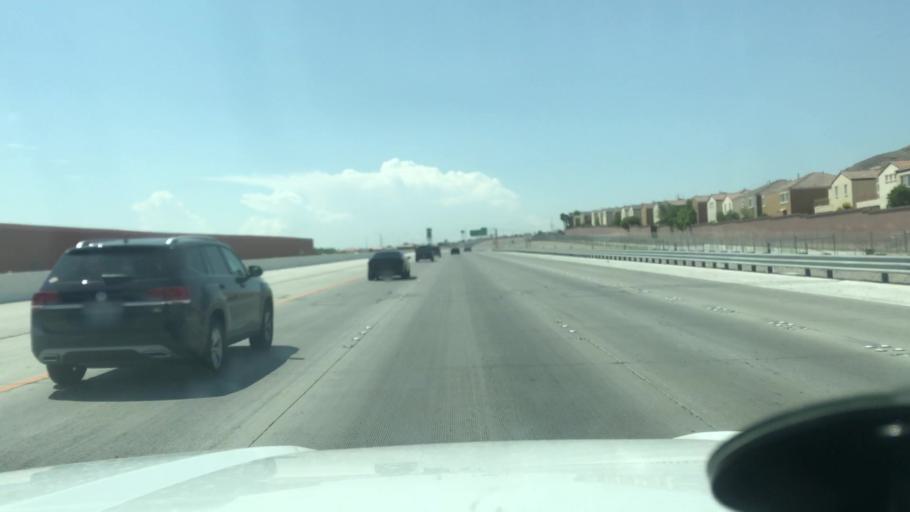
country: US
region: Nevada
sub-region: Clark County
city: Summerlin South
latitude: 36.2288
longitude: -115.3256
